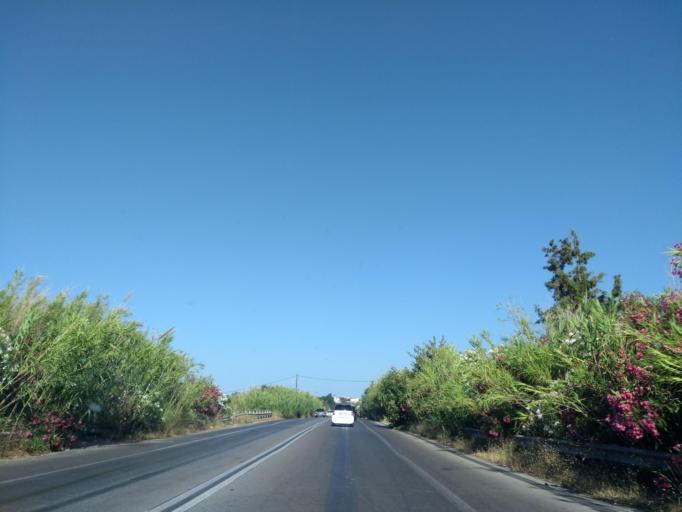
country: GR
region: Crete
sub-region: Nomos Chanias
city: Daratsos
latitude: 35.5057
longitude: 23.9727
